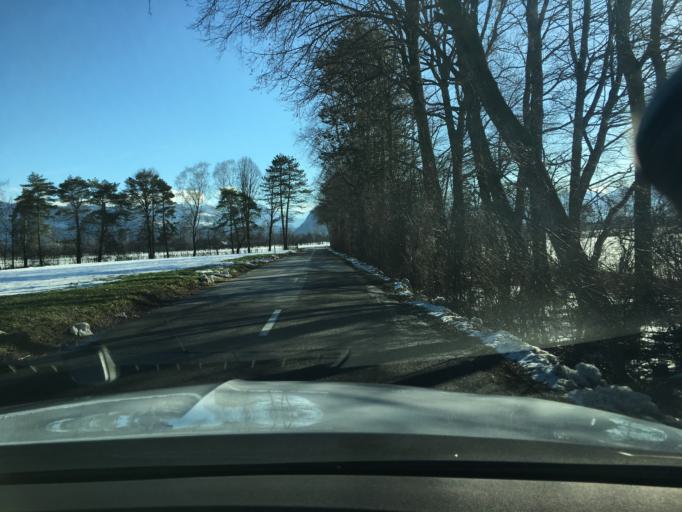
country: CH
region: Saint Gallen
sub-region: Wahlkreis Rheintal
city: Rebstein
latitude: 47.3731
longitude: 9.5908
